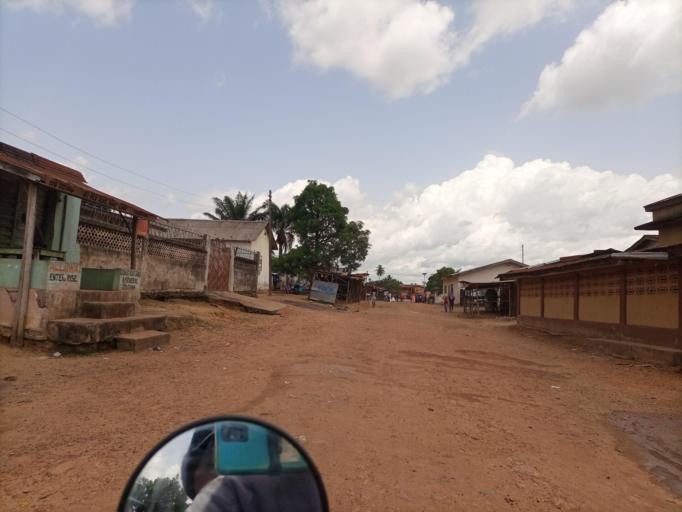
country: SL
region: Southern Province
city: Bo
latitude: 7.9592
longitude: -11.7340
